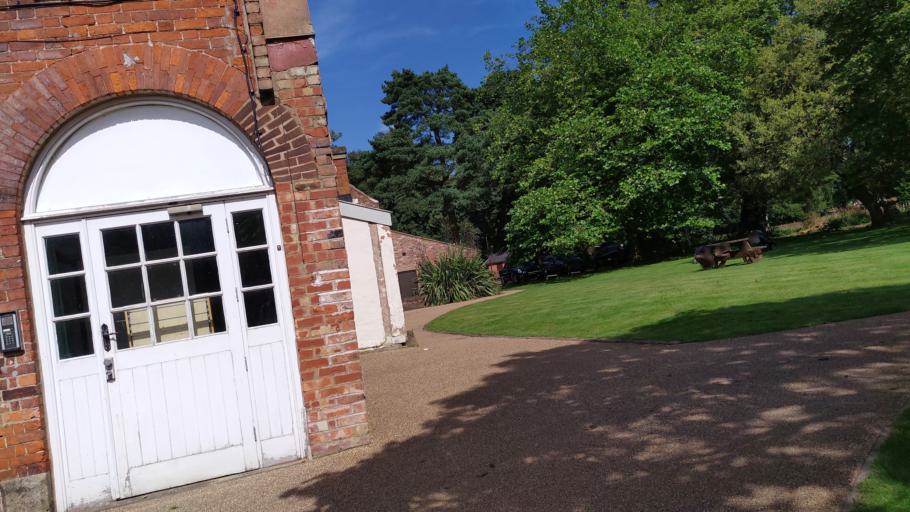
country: GB
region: England
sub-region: Lancashire
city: Leyland
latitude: 53.6821
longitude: -2.7021
